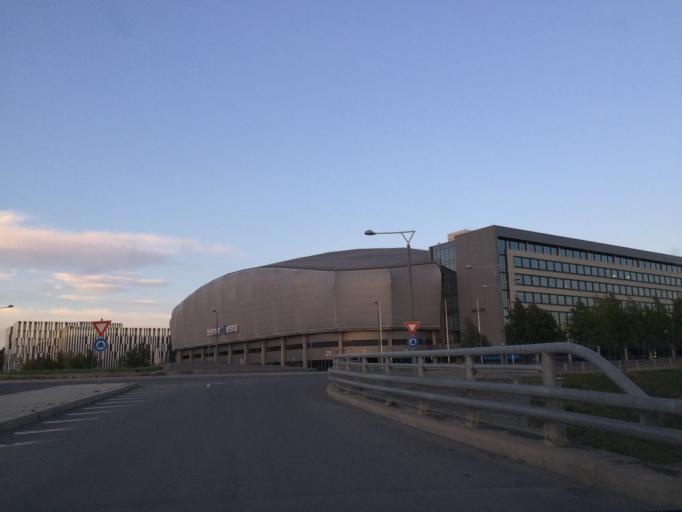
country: NO
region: Akershus
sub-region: Baerum
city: Lysaker
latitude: 59.9028
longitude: 10.6201
